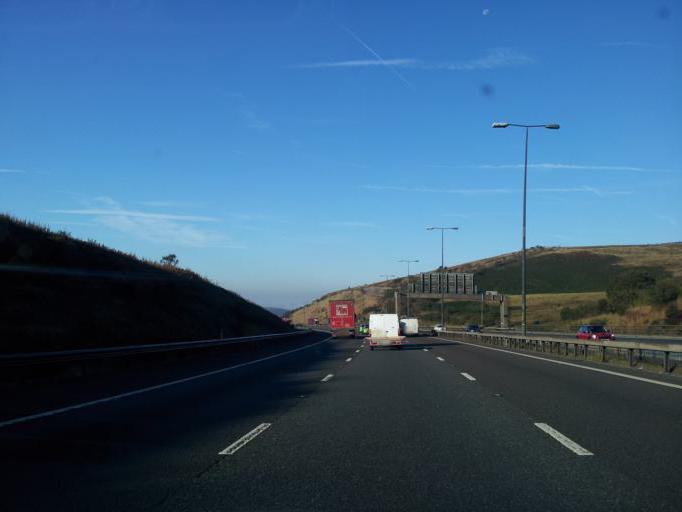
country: GB
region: England
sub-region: Borough of Rochdale
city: Littleborough
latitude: 53.6289
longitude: -2.0370
